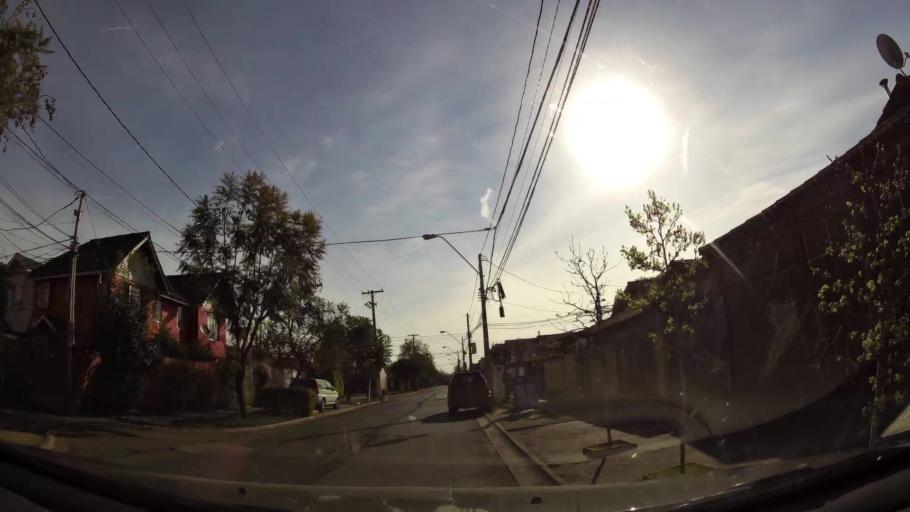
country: CL
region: Santiago Metropolitan
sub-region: Provincia de Cordillera
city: Puente Alto
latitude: -33.5833
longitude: -70.5613
